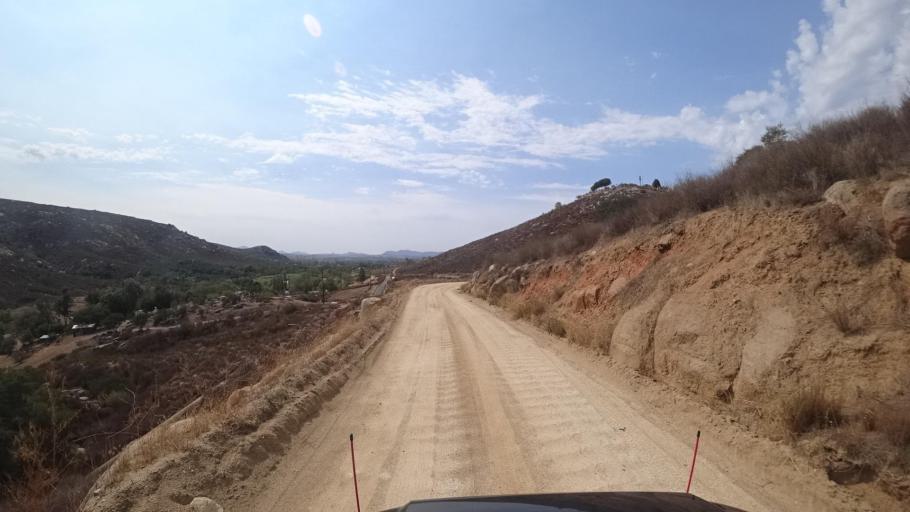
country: US
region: California
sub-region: San Diego County
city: Ramona
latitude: 33.0960
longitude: -116.8297
